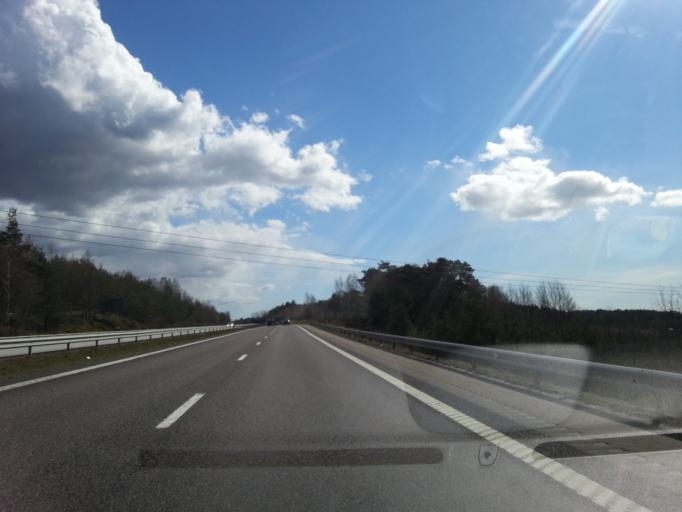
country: SE
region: Vaestra Goetaland
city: Svanesund
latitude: 58.0962
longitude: 11.8822
